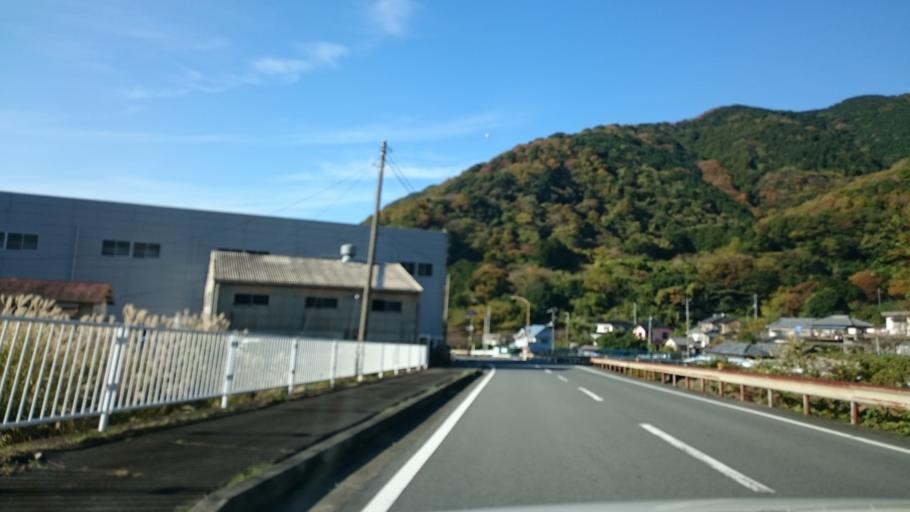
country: JP
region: Shizuoka
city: Heda
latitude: 34.9689
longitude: 138.7995
